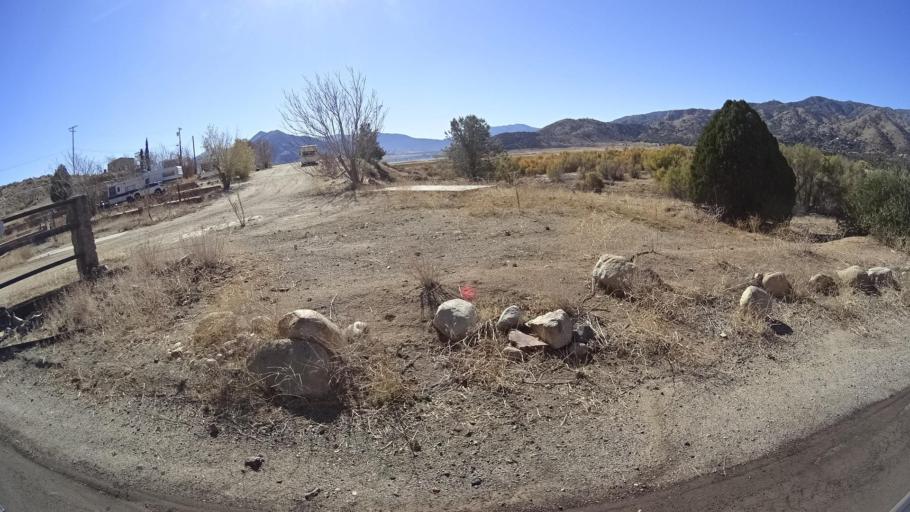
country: US
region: California
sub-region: Kern County
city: Wofford Heights
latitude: 35.7039
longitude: -118.4461
